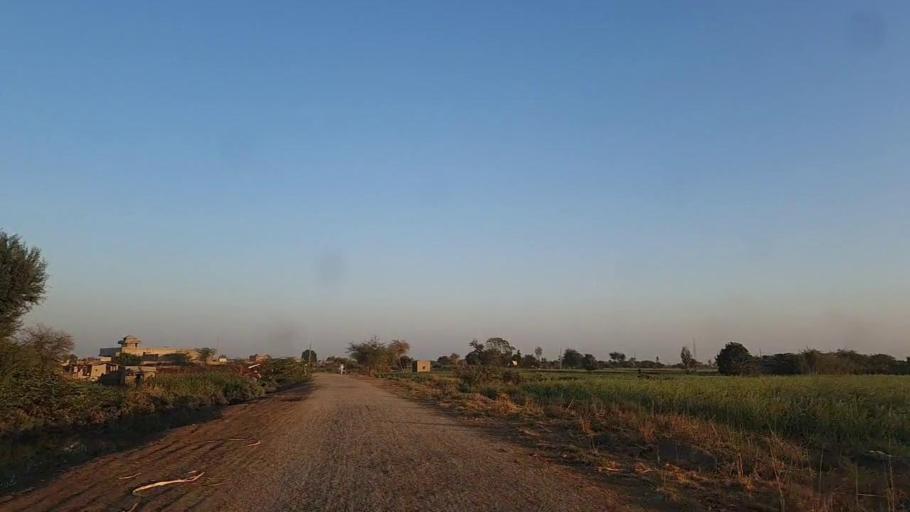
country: PK
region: Sindh
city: Samaro
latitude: 25.2985
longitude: 69.3825
